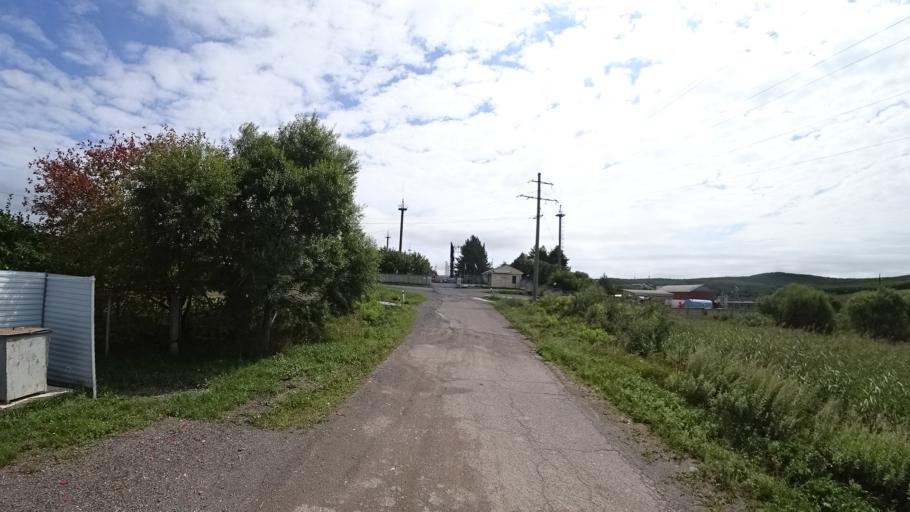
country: RU
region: Primorskiy
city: Lyalichi
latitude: 44.1306
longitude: 132.3885
